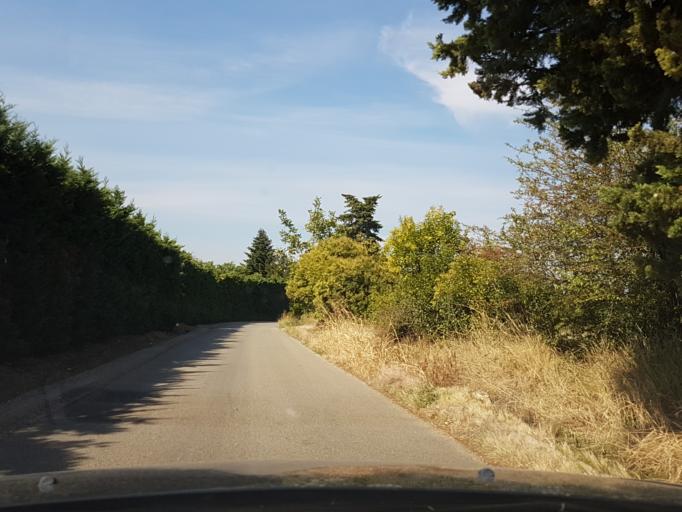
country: FR
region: Provence-Alpes-Cote d'Azur
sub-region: Departement des Bouches-du-Rhone
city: Eygalieres
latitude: 43.7824
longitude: 4.9237
